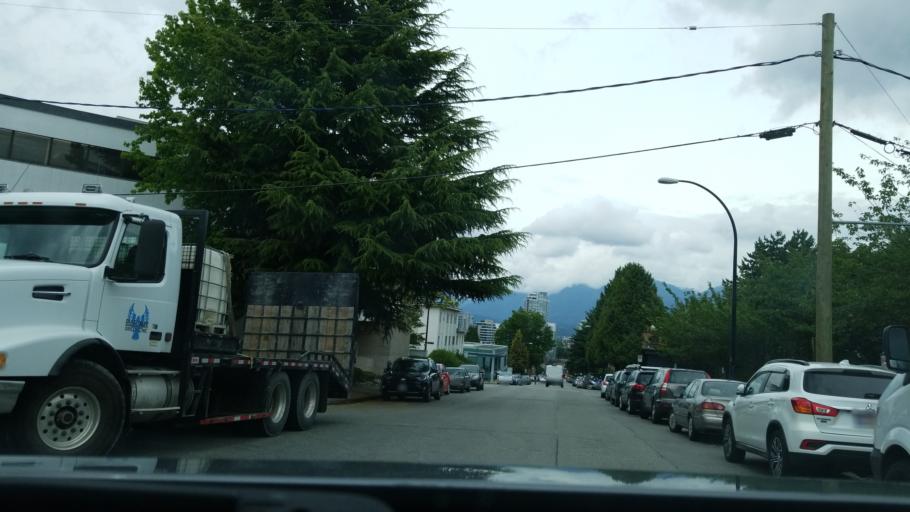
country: CA
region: British Columbia
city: Vancouver
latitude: 49.2631
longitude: -123.1030
